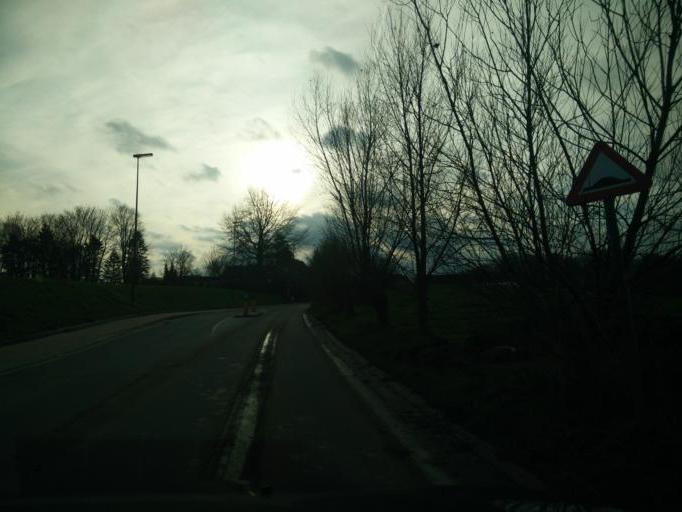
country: BE
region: Flanders
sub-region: Provincie Oost-Vlaanderen
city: Merelbeke
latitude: 50.9751
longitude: 3.7206
